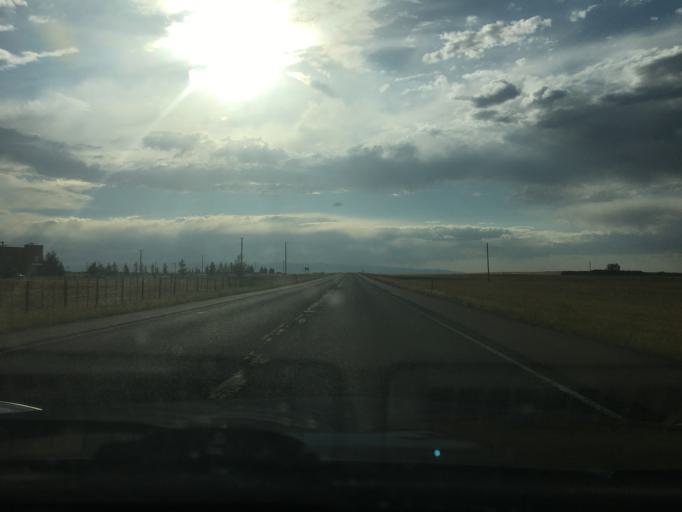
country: US
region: Wyoming
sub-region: Albany County
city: Laramie
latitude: 41.3227
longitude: -105.6628
